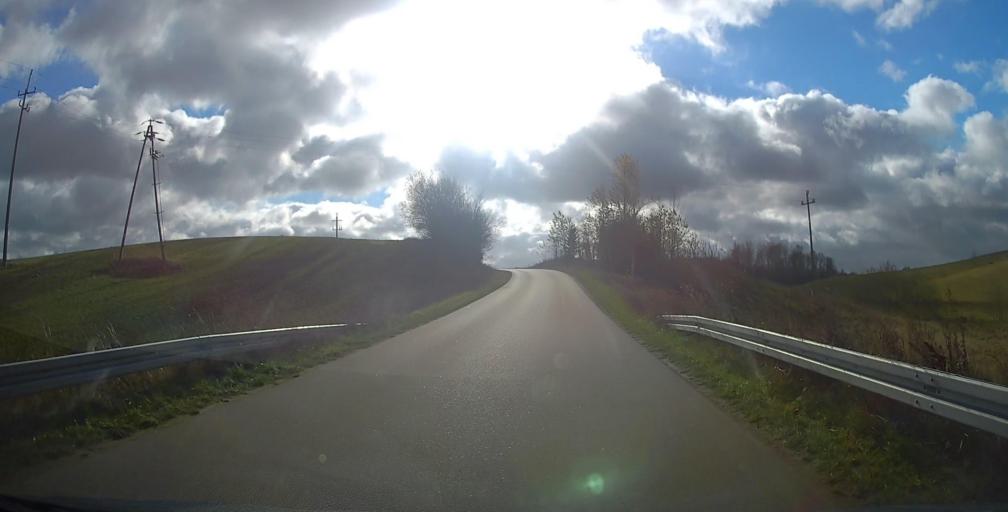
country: PL
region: Podlasie
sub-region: Suwalki
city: Suwalki
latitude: 54.3256
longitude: 22.8624
